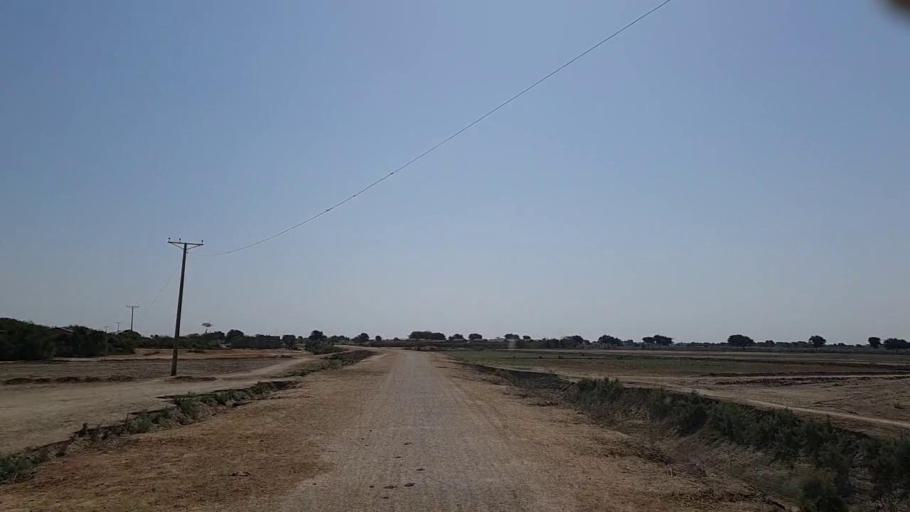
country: PK
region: Sindh
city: Mirpur Batoro
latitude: 24.6793
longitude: 68.3015
